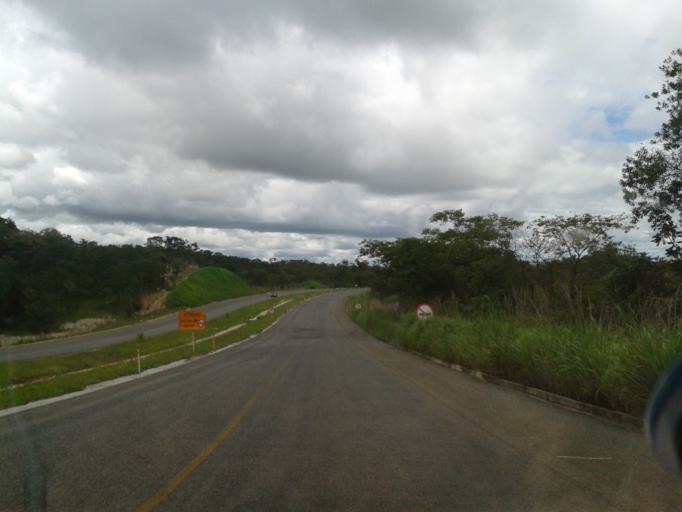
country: BR
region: Goias
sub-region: Goias
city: Goias
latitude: -16.0016
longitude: -50.0688
